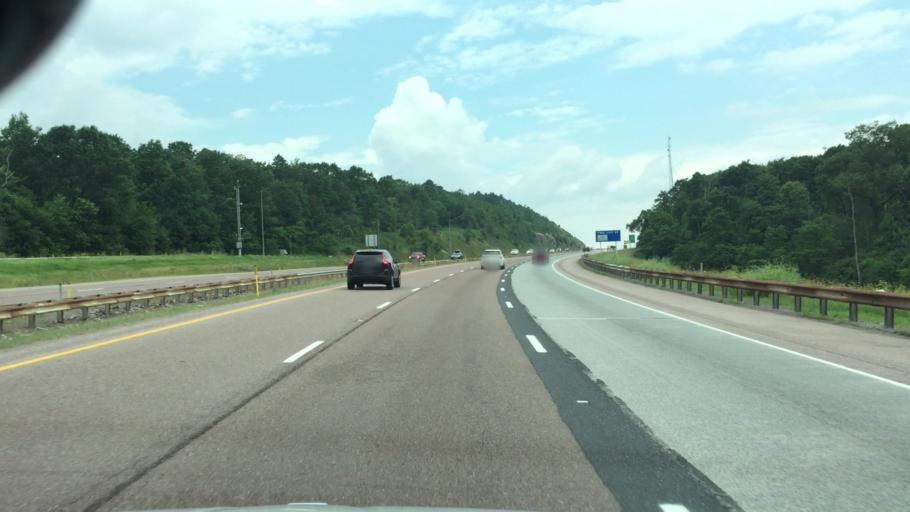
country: US
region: Maryland
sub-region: Allegany County
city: Frostburg
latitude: 39.6649
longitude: -78.9604
